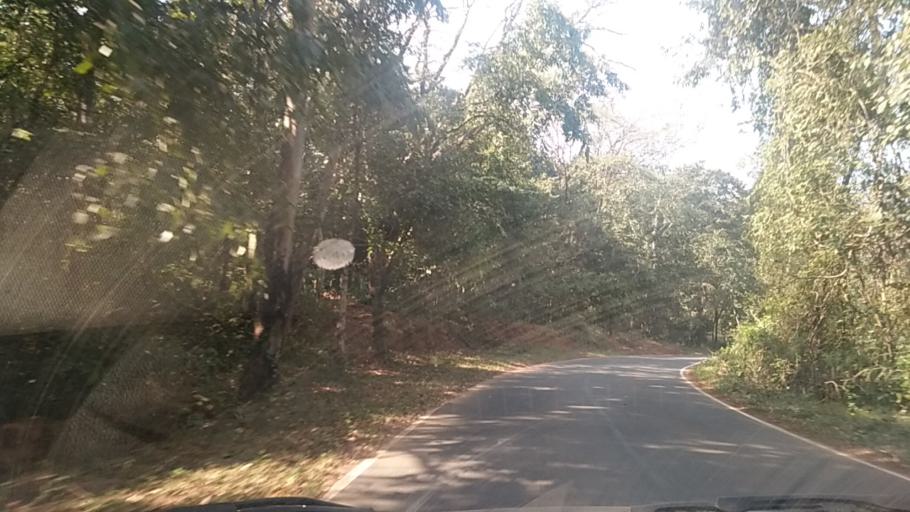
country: IN
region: Goa
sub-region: South Goa
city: Sanguem
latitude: 15.2124
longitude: 74.2082
